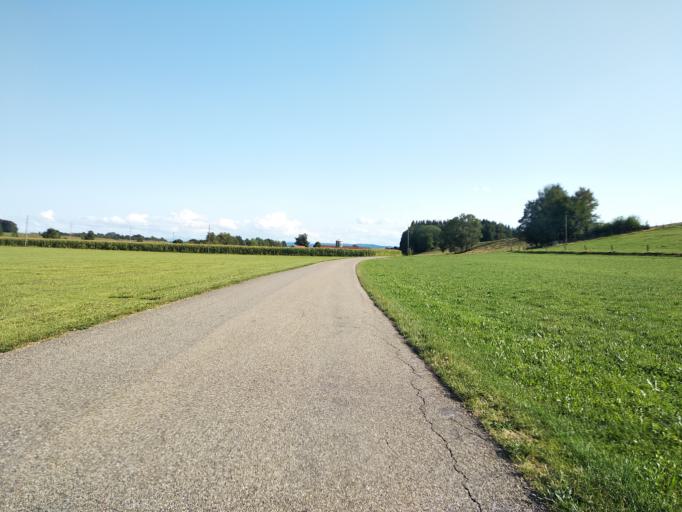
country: DE
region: Bavaria
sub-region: Swabia
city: Lautrach
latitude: 47.8844
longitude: 10.1155
